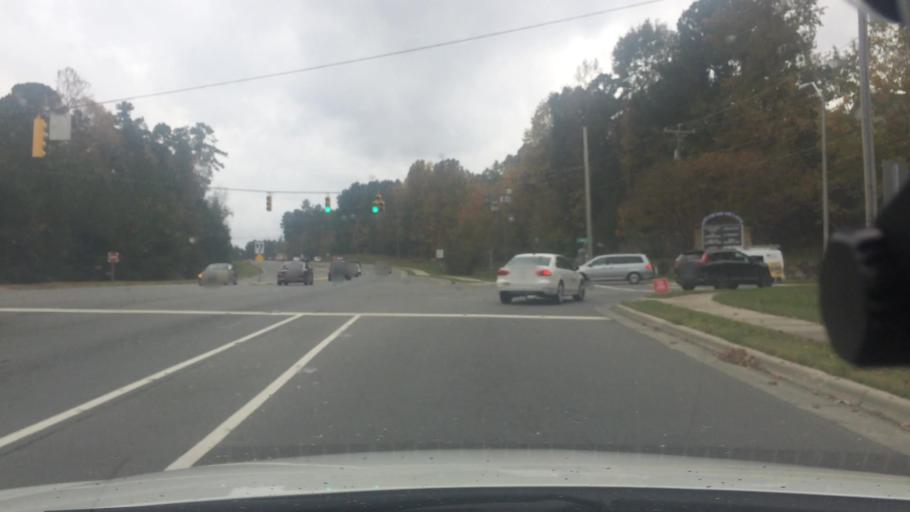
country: US
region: North Carolina
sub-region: Orange County
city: Carrboro
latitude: 35.8794
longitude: -79.0637
